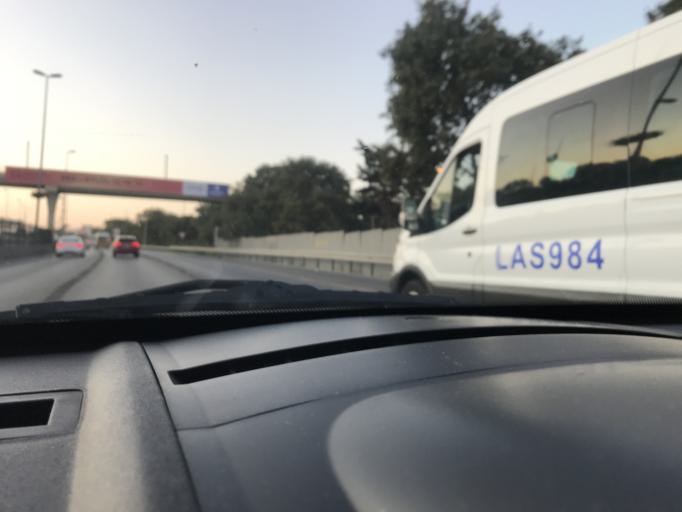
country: TR
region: Istanbul
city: UEskuedar
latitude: 41.0211
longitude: 29.0486
